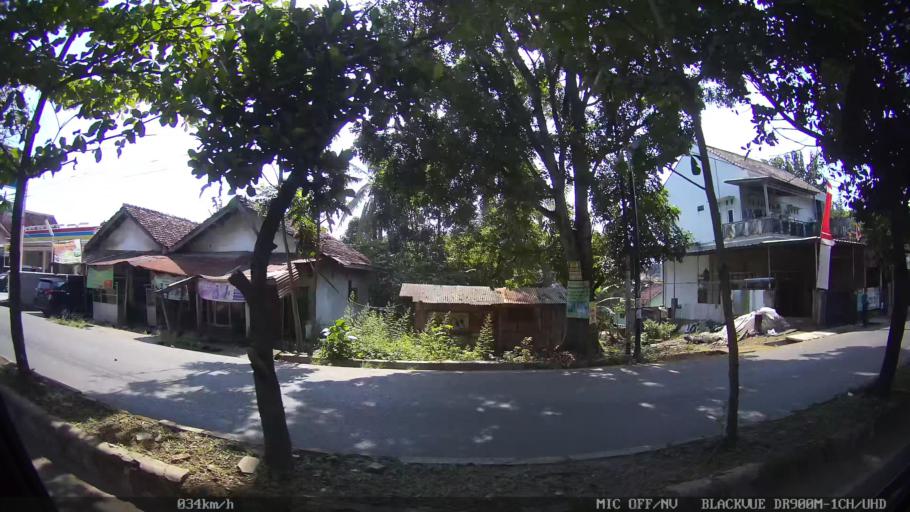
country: ID
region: Lampung
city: Kedaton
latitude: -5.3652
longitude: 105.2349
